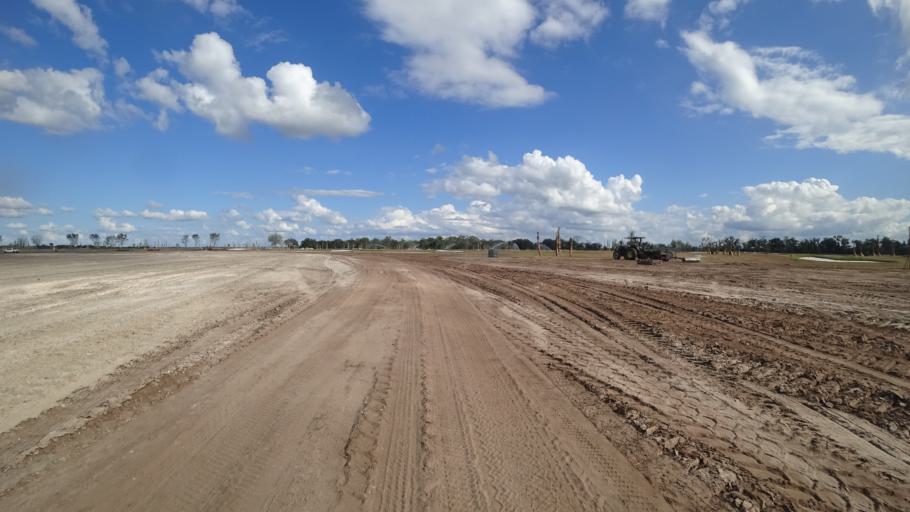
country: US
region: Florida
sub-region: Sarasota County
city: The Meadows
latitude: 27.4639
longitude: -82.3921
